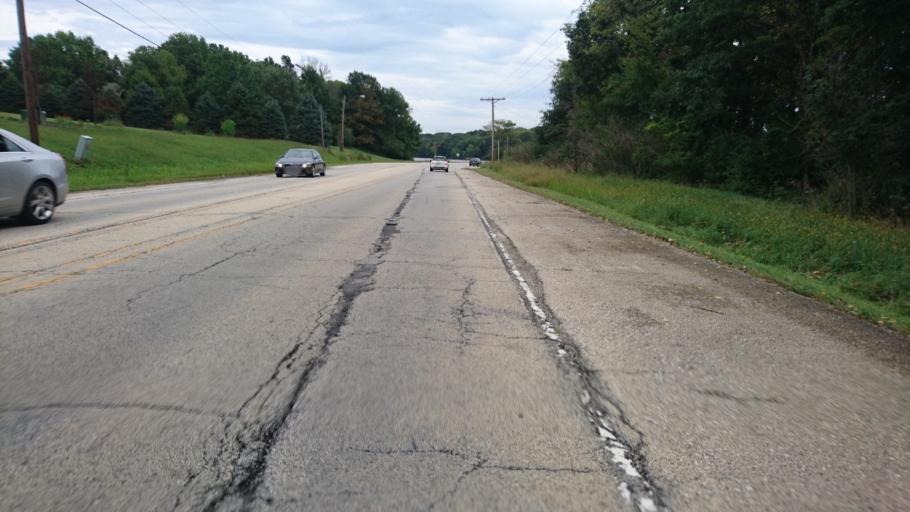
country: US
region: Illinois
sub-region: Sangamon County
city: Chatham
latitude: 39.6768
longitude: -89.6697
